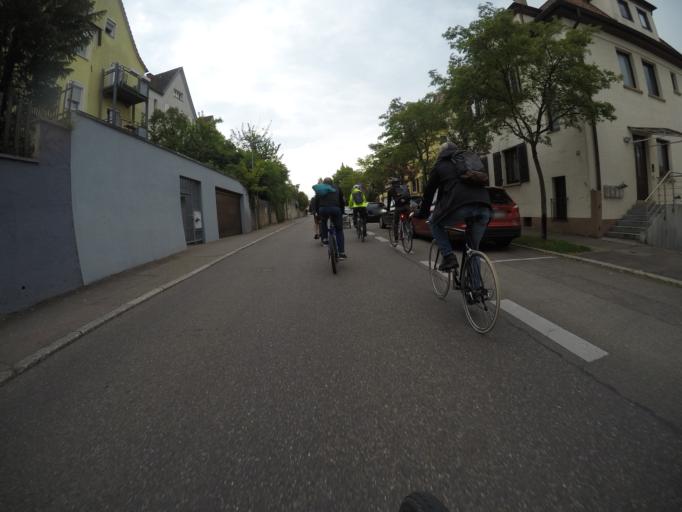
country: DE
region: Baden-Wuerttemberg
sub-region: Regierungsbezirk Stuttgart
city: Esslingen
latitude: 48.7357
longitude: 9.3256
